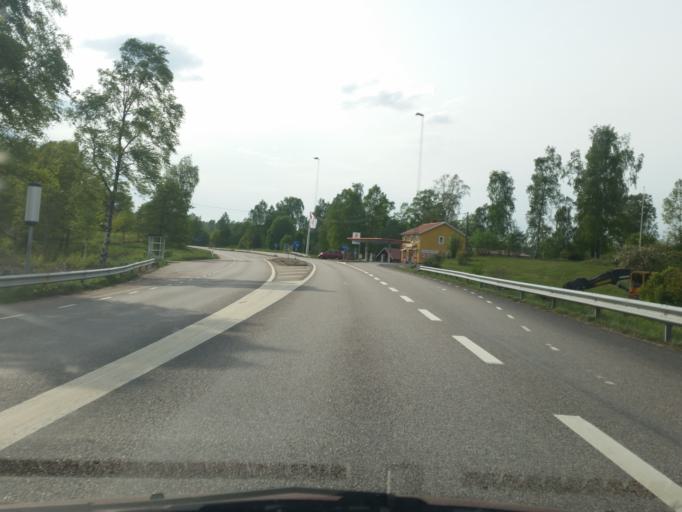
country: SE
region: Vaestra Goetaland
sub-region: Ulricehamns Kommun
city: Ulricehamn
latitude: 57.8133
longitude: 13.2908
